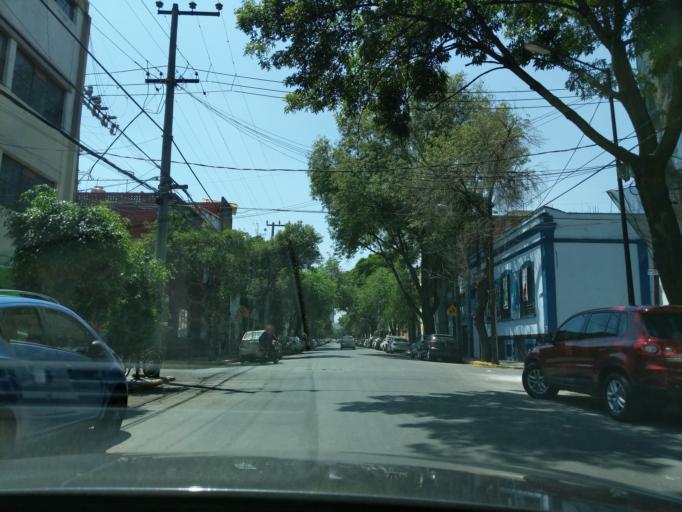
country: MX
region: Mexico City
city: Cuauhtemoc
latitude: 19.4458
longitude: -99.1630
